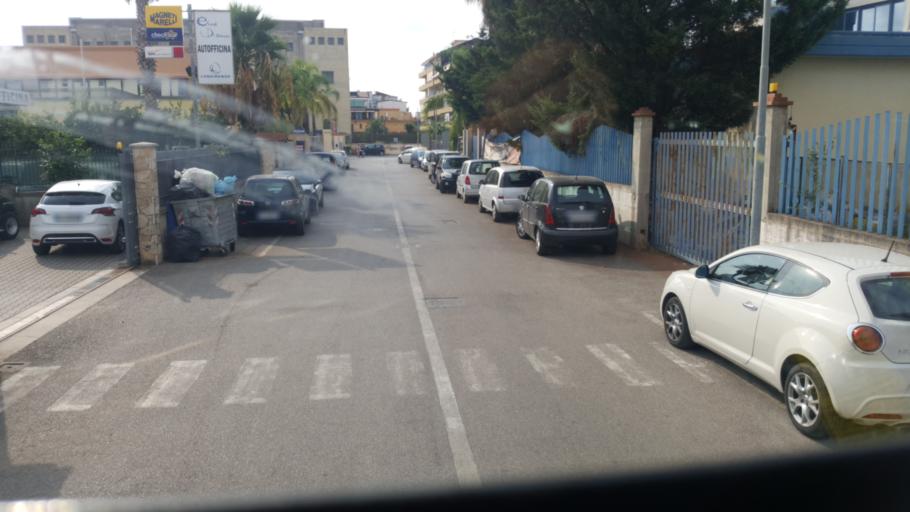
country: IT
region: Campania
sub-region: Provincia di Salerno
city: Battipaglia
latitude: 40.5981
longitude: 14.9858
